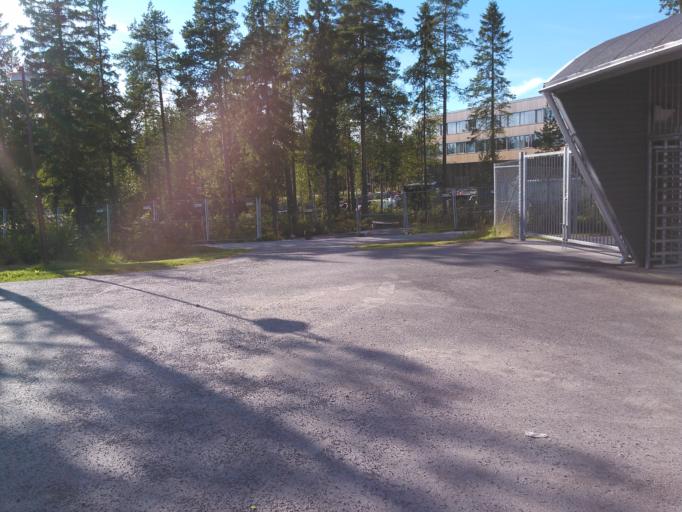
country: SE
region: Vaesterbotten
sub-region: Umea Kommun
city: Umea
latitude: 63.8210
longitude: 20.3194
